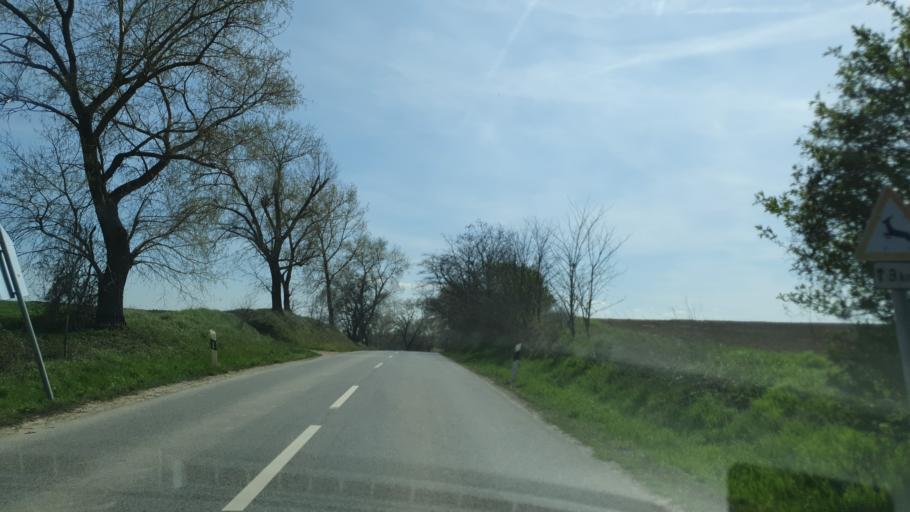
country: HU
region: Komarom-Esztergom
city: Bokod
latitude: 47.4883
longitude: 18.2418
